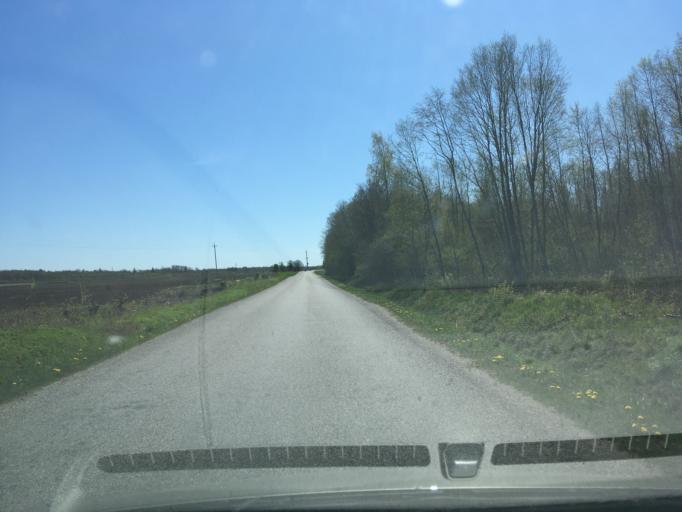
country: EE
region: Harju
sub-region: Raasiku vald
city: Arukula
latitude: 59.4015
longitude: 25.0785
